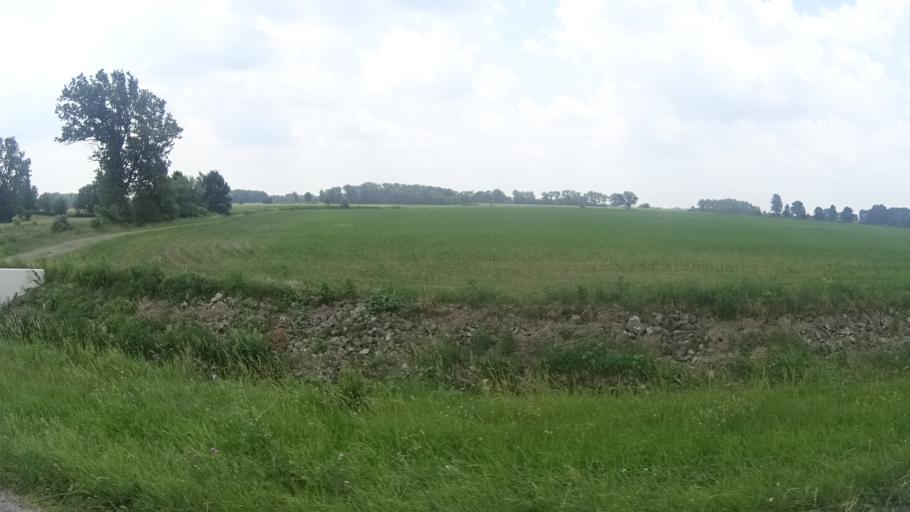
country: US
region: Ohio
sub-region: Erie County
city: Milan
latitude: 41.3231
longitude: -82.6790
